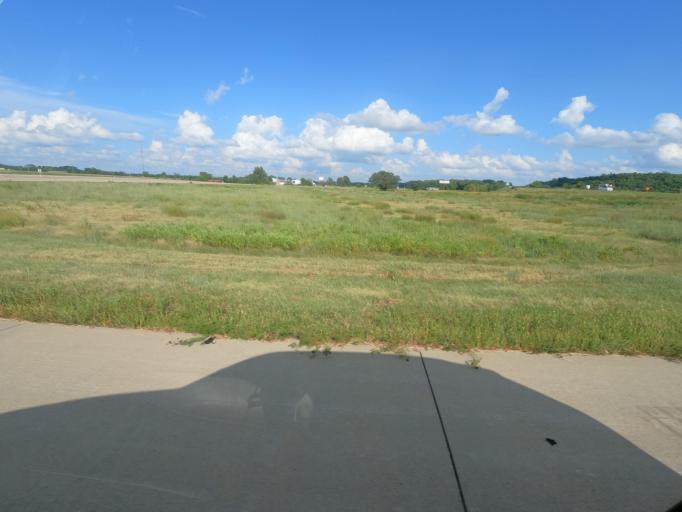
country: US
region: Kansas
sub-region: Wabaunsee County
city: Alma
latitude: 39.0665
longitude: -96.1908
